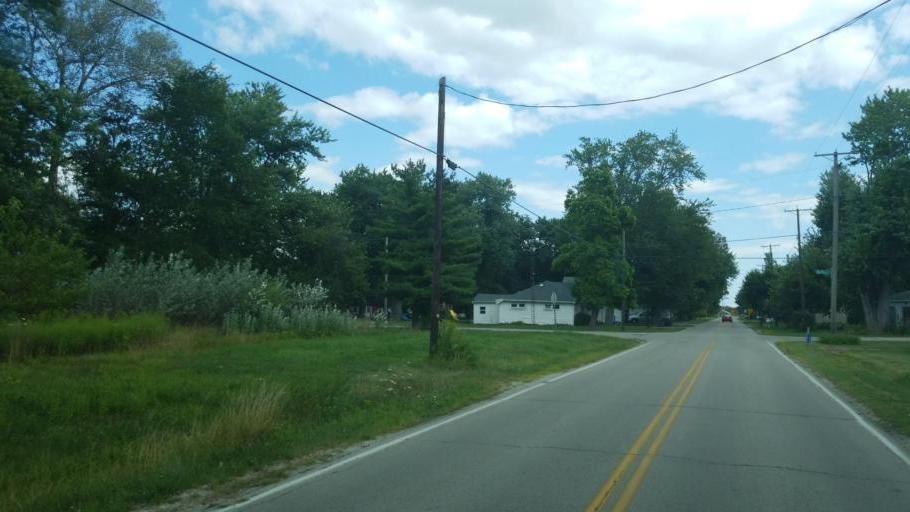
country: US
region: Ohio
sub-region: Lucas County
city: Curtice
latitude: 41.6612
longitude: -83.2625
